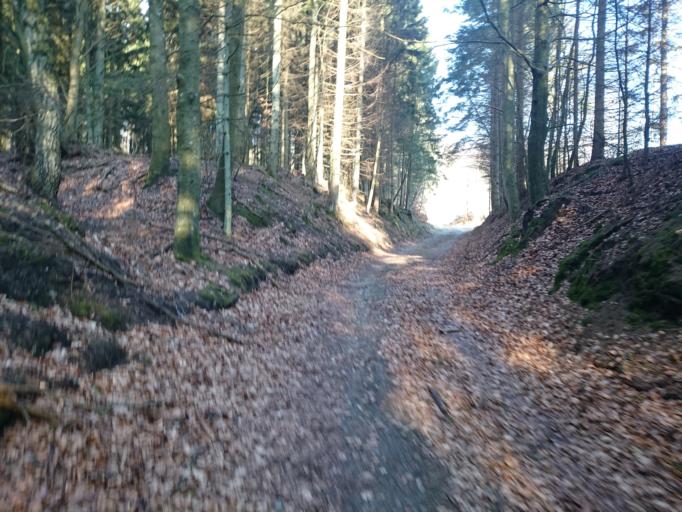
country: SE
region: Skane
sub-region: Sjobo Kommun
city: Sjoebo
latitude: 55.6025
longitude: 13.7655
